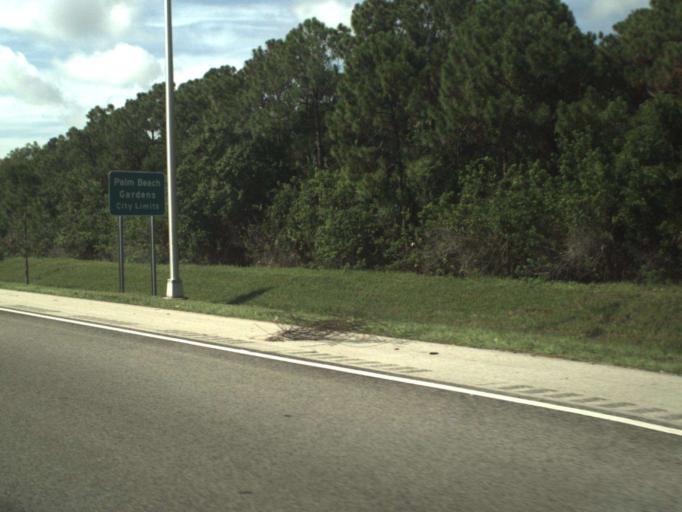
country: US
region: Florida
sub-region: Palm Beach County
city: Palm Beach Gardens
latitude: 26.8748
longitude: -80.1239
